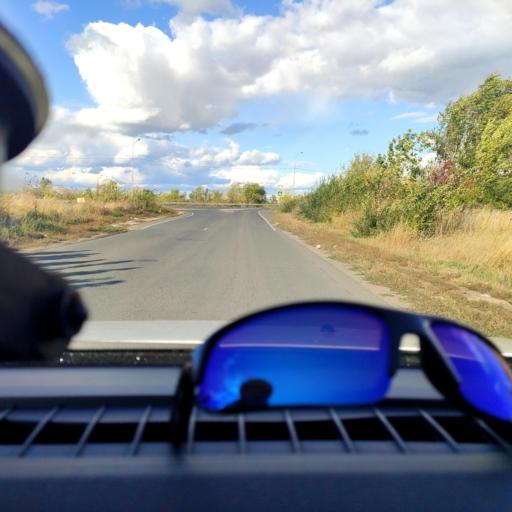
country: RU
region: Samara
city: Chapayevsk
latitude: 52.9956
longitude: 49.7340
